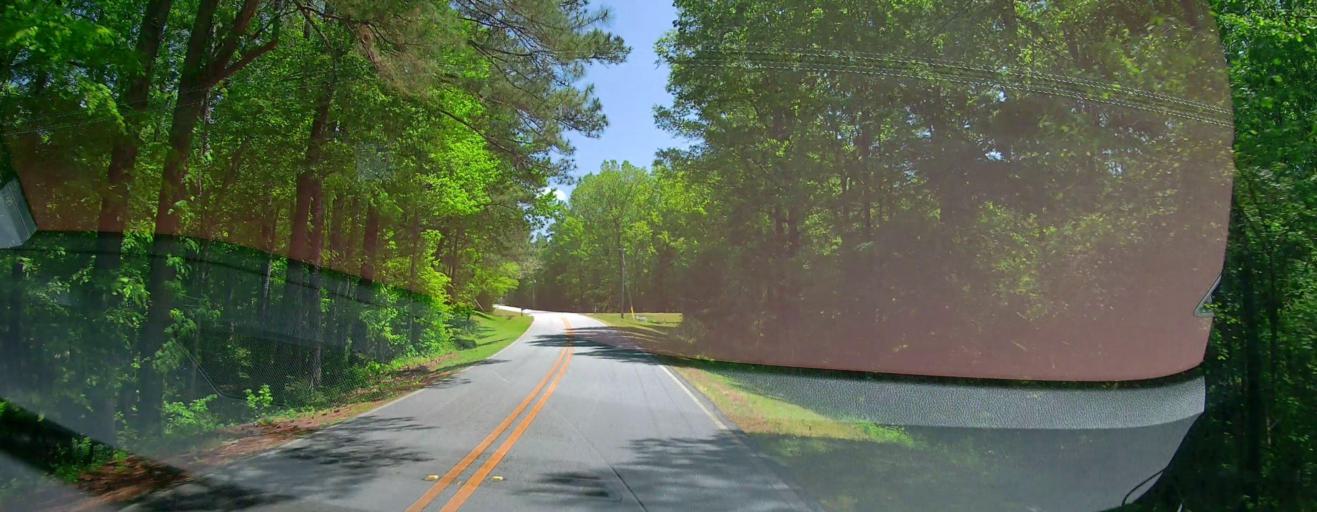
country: US
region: Georgia
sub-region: Jones County
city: Gray
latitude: 32.9668
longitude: -83.5519
